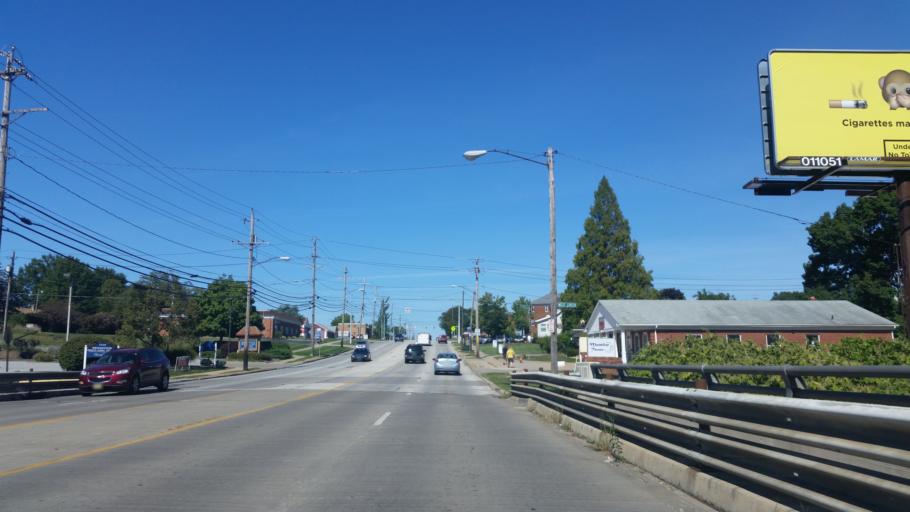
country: US
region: Ohio
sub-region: Cuyahoga County
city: Brooklyn Heights
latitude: 41.4112
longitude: -81.6928
